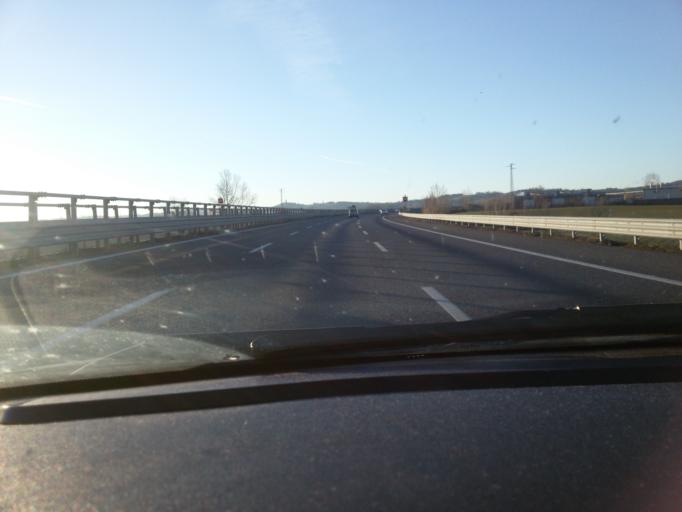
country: IT
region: Piedmont
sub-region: Provincia di Alessandria
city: Mirabello Monferrato
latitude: 45.0309
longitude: 8.5364
